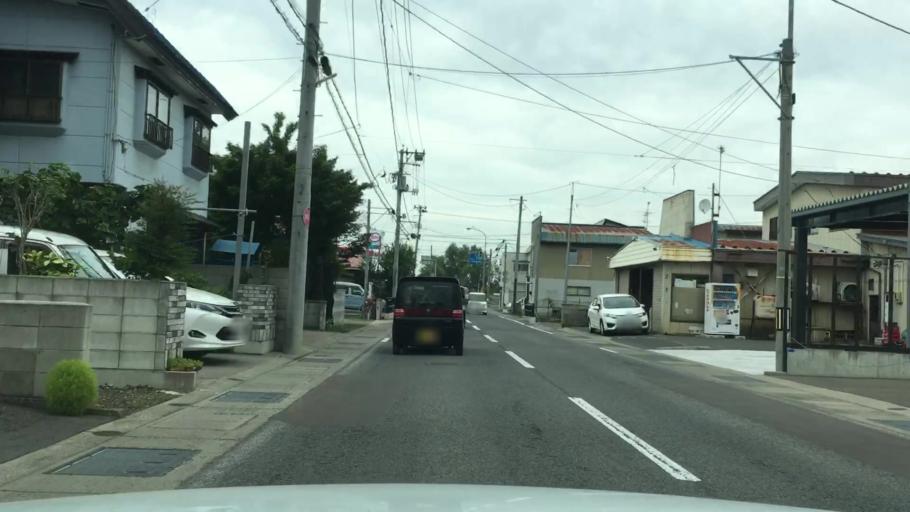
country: JP
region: Aomori
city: Hirosaki
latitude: 40.6136
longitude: 140.4620
